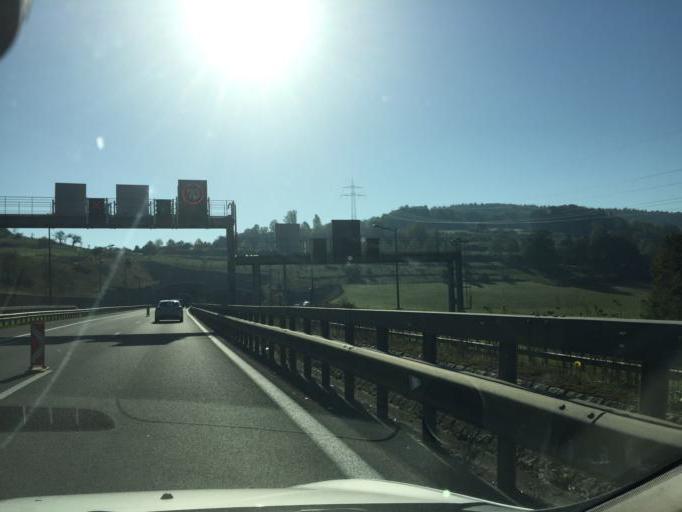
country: LU
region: Luxembourg
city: Rollingen
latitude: 49.7326
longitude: 6.1030
